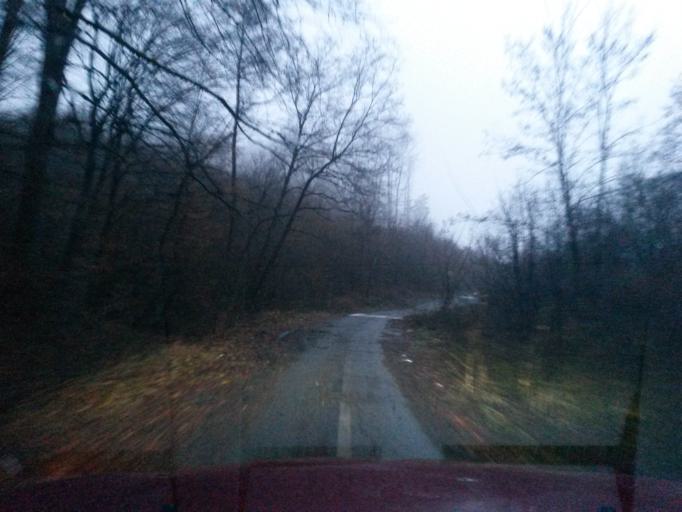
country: SK
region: Presovsky
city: Stropkov
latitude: 49.1461
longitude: 21.6544
